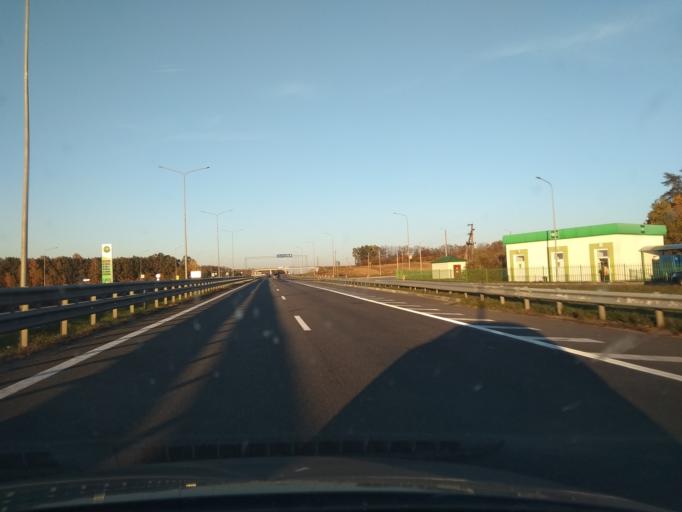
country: BY
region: Brest
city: Baranovichi
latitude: 53.1915
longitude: 26.0758
